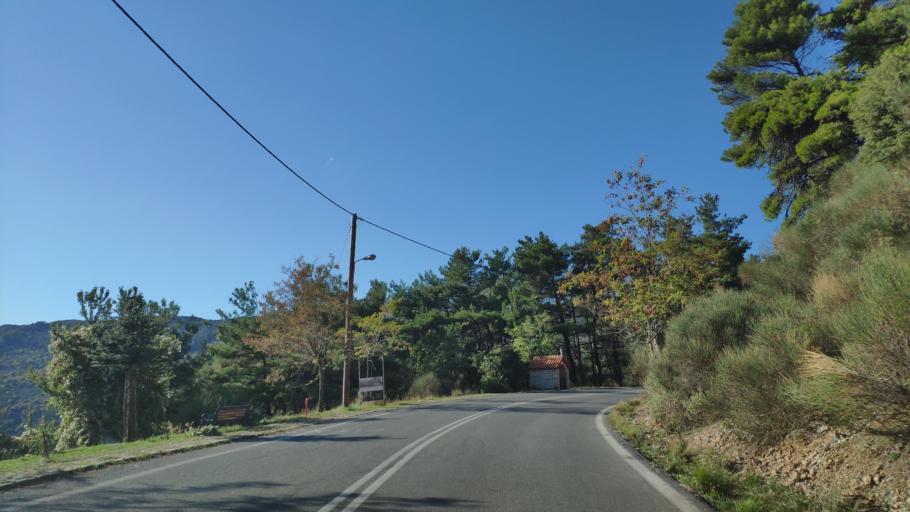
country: GR
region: Peloponnese
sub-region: Nomos Arkadias
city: Dimitsana
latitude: 37.5886
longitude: 22.0444
